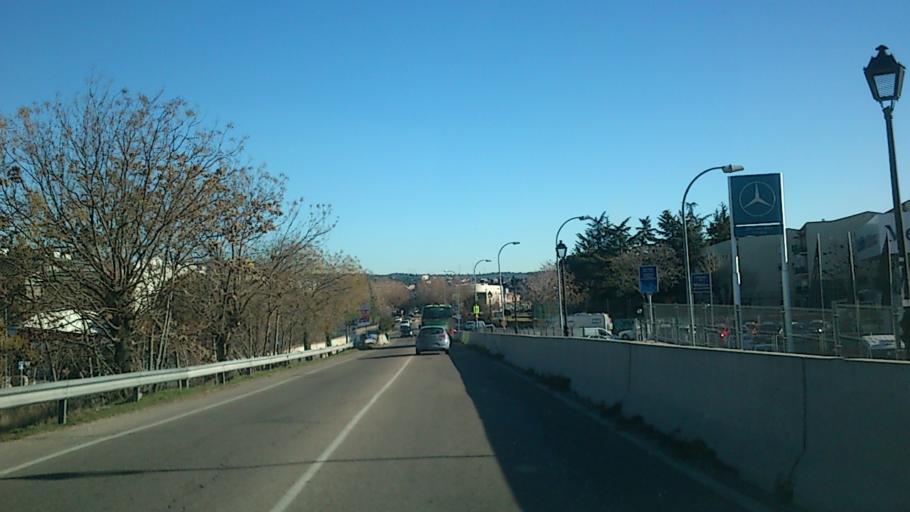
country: ES
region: Madrid
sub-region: Provincia de Madrid
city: Collado-Villalba
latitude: 40.6375
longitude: -4.0206
